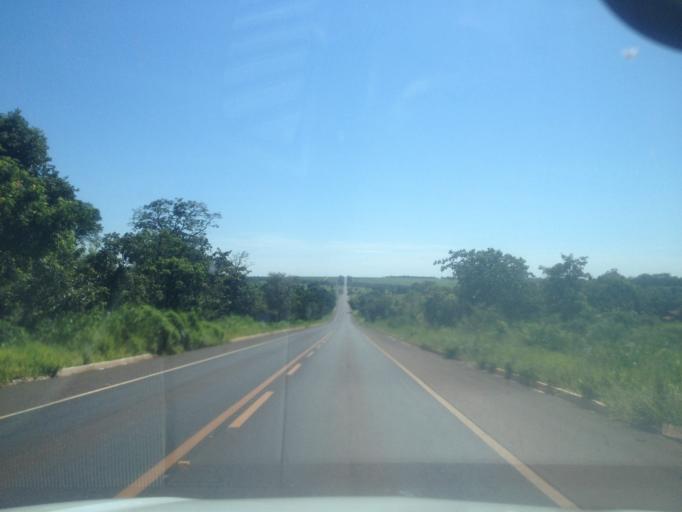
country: BR
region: Minas Gerais
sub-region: Santa Vitoria
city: Santa Vitoria
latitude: -18.9085
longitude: -50.2133
